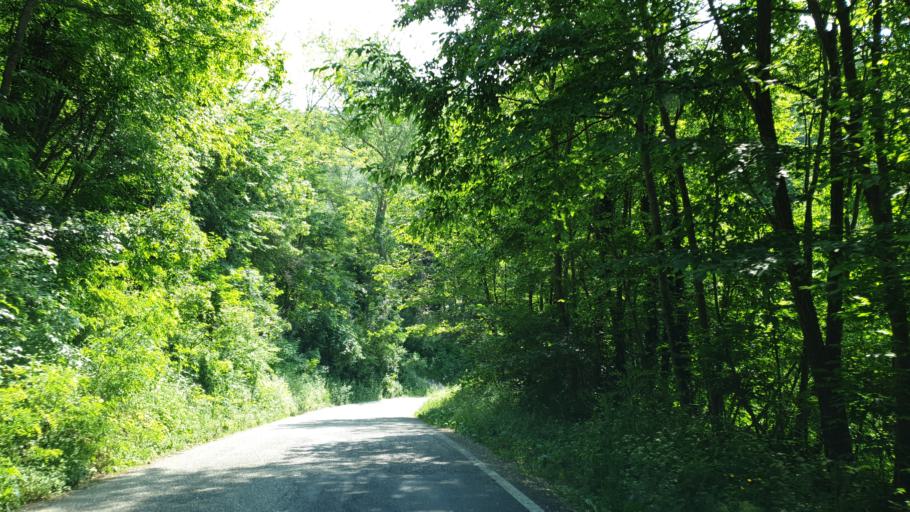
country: IT
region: Emilia-Romagna
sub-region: Forli-Cesena
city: Sarsina
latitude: 43.9131
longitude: 12.1707
